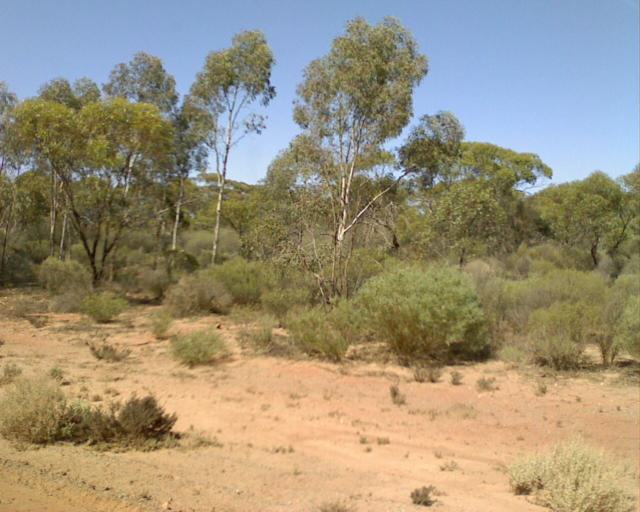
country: AU
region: Western Australia
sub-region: Kalgoorlie/Boulder
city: Boulder
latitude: -30.8274
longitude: 121.3800
